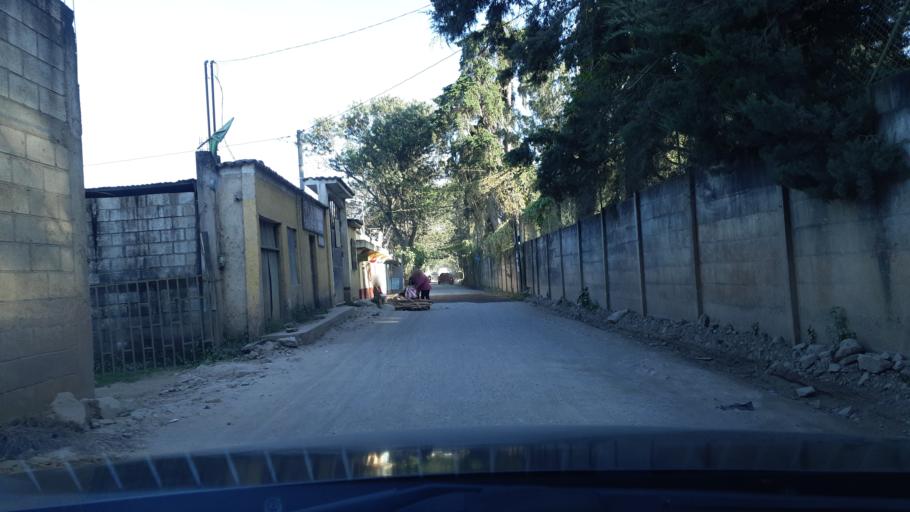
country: GT
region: Chimaltenango
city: El Tejar
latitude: 14.6402
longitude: -90.8070
